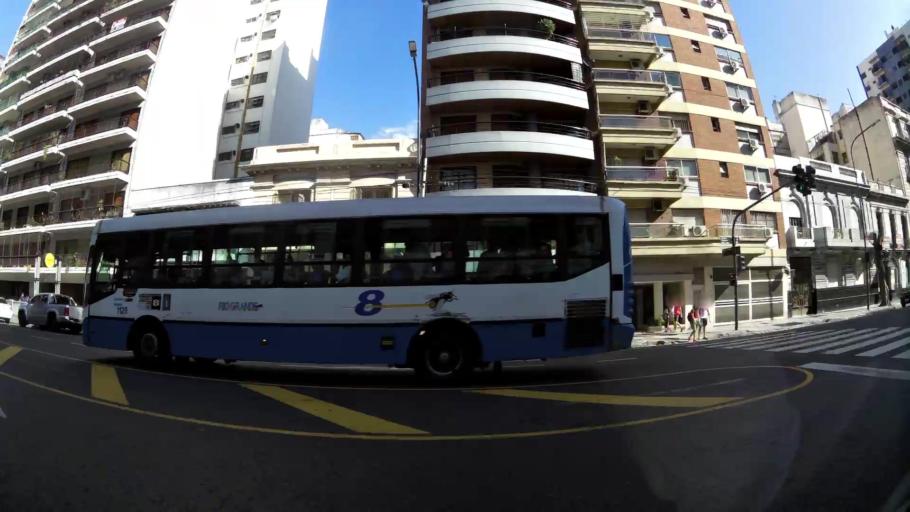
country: AR
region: Buenos Aires F.D.
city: Villa Santa Rita
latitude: -34.6239
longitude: -58.4492
